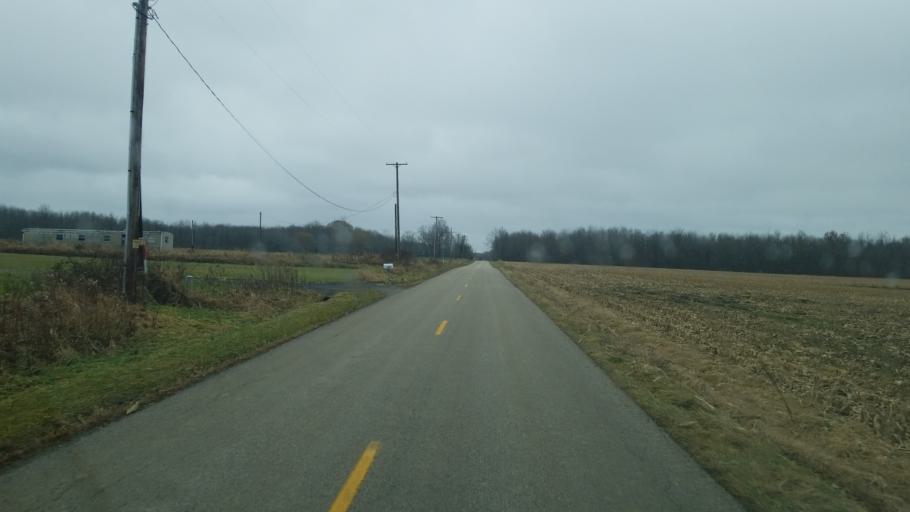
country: US
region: Ohio
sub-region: Ashtabula County
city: Roaming Shores
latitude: 41.5972
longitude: -80.7630
